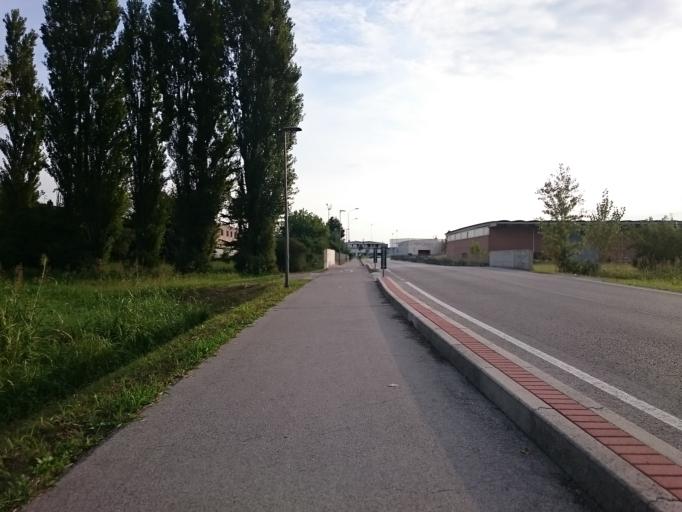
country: IT
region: Veneto
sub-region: Provincia di Vicenza
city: Camisano Vicentino
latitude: 45.5194
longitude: 11.7007
